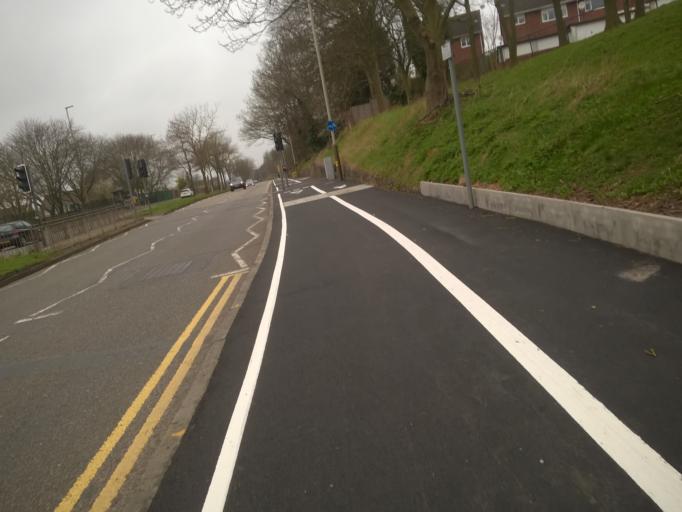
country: GB
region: England
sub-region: City of Leicester
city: Leicester
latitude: 52.6476
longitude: -1.1596
